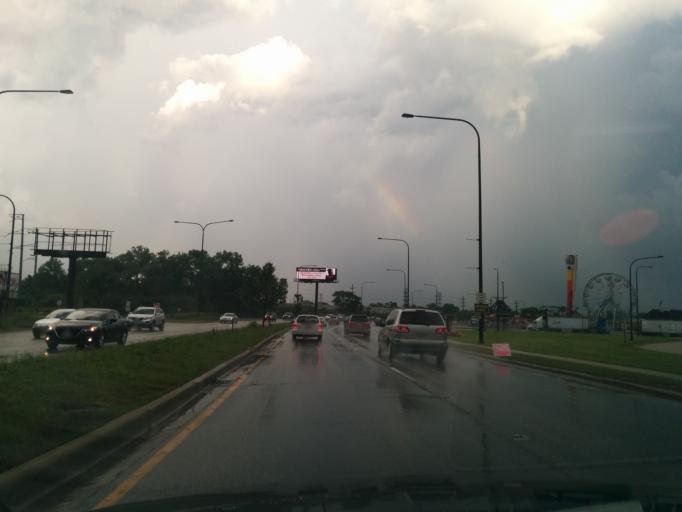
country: US
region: Illinois
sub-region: Cook County
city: Bridgeview
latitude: 41.7670
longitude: -87.8028
